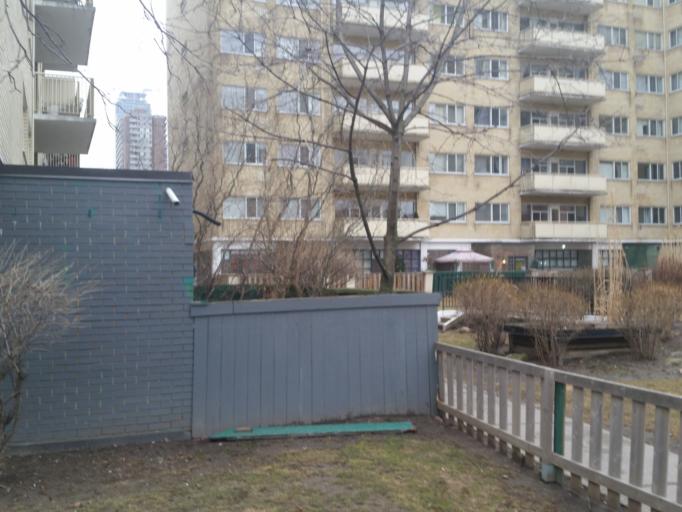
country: CA
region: Ontario
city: Toronto
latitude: 43.6683
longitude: -79.3793
